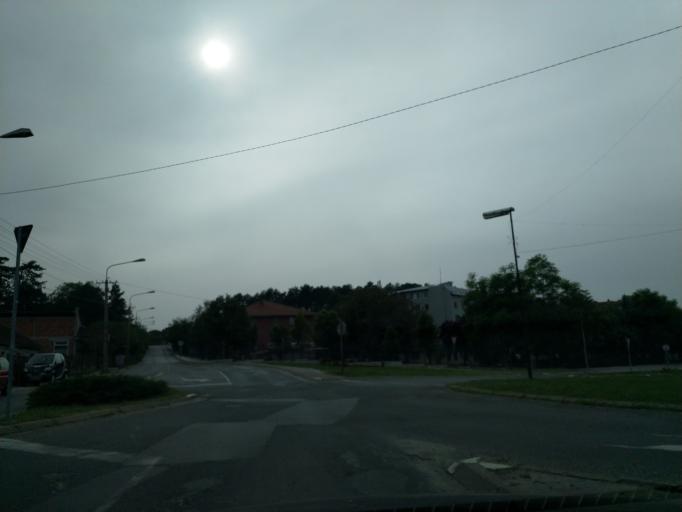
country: RS
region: Central Serbia
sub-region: Pomoravski Okrug
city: Jagodina
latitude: 43.9770
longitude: 21.2497
